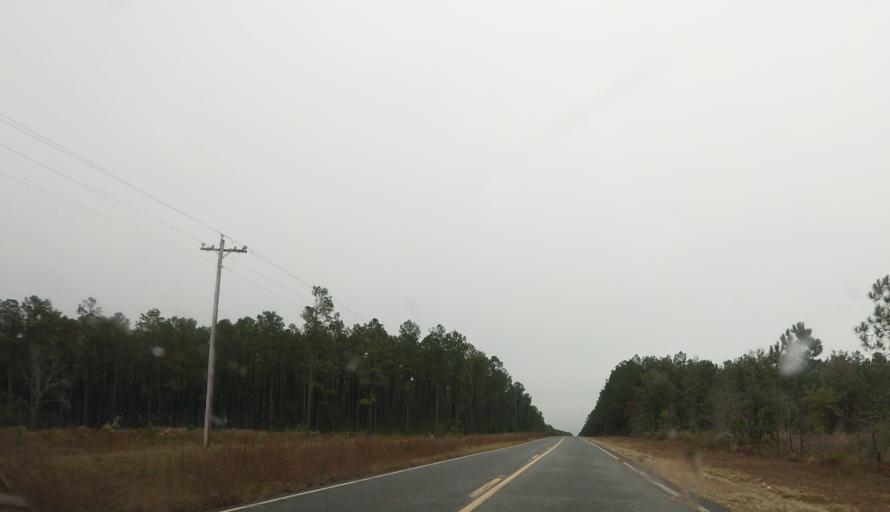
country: US
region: Georgia
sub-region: Taylor County
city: Butler
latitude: 32.4351
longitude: -84.3412
